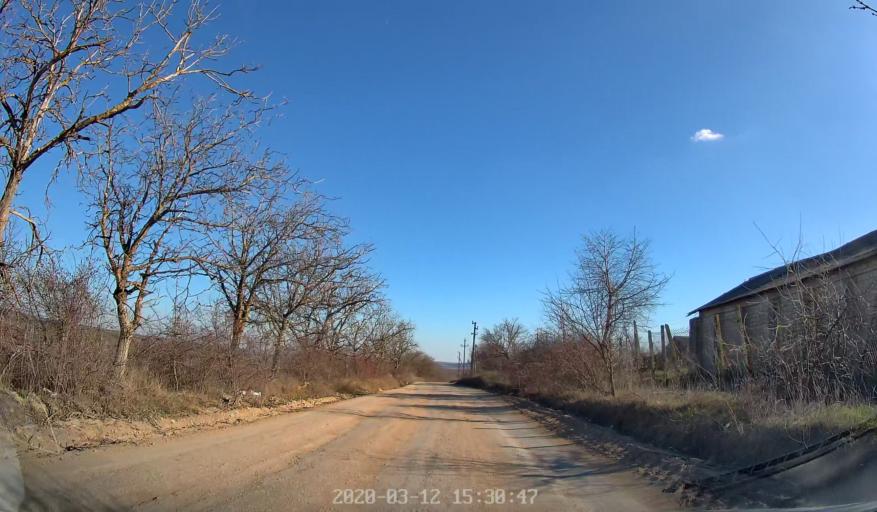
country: MD
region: Chisinau
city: Ciorescu
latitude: 47.1597
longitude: 28.9401
